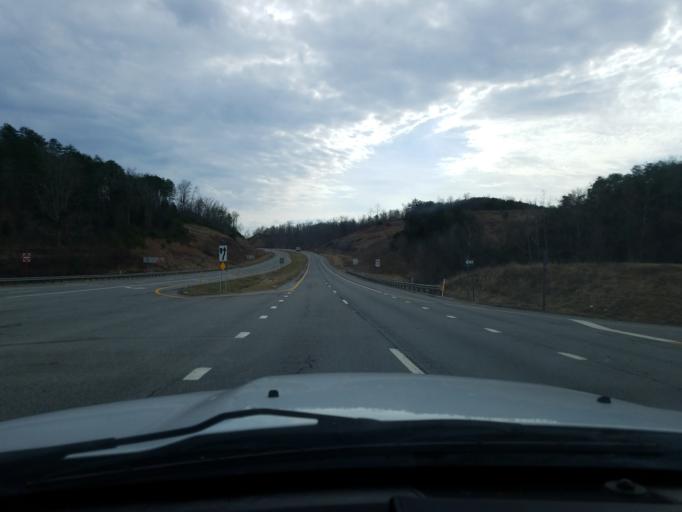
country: US
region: West Virginia
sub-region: Putnam County
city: Buffalo
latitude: 38.5680
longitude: -82.0136
